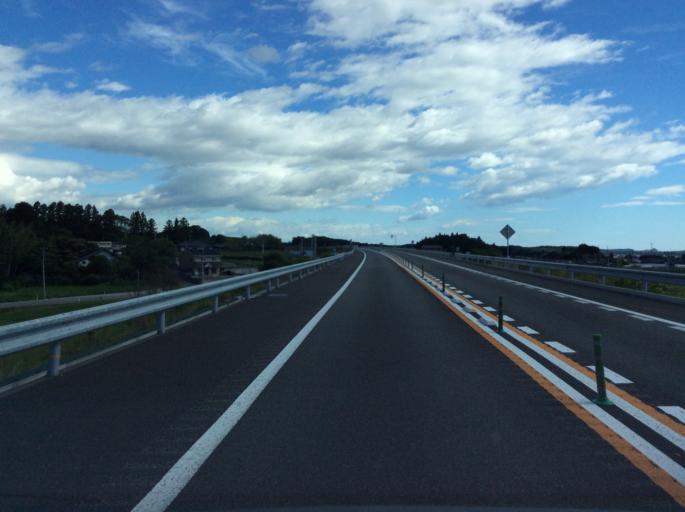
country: JP
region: Fukushima
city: Namie
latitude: 37.6147
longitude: 140.9273
